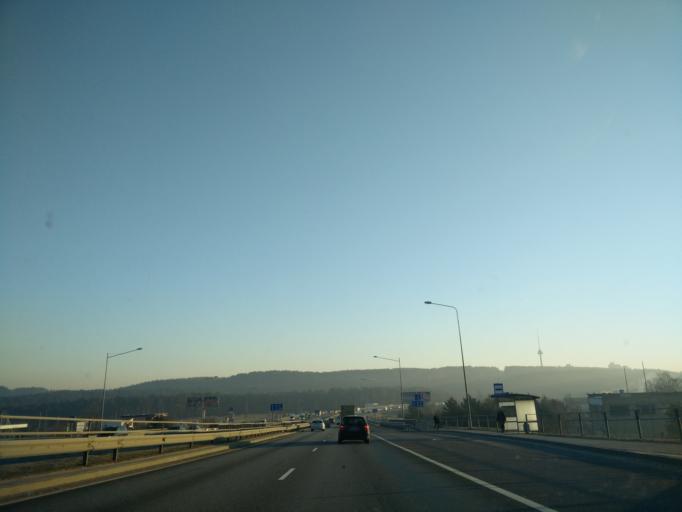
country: LT
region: Vilnius County
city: Lazdynai
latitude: 54.6651
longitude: 25.1734
